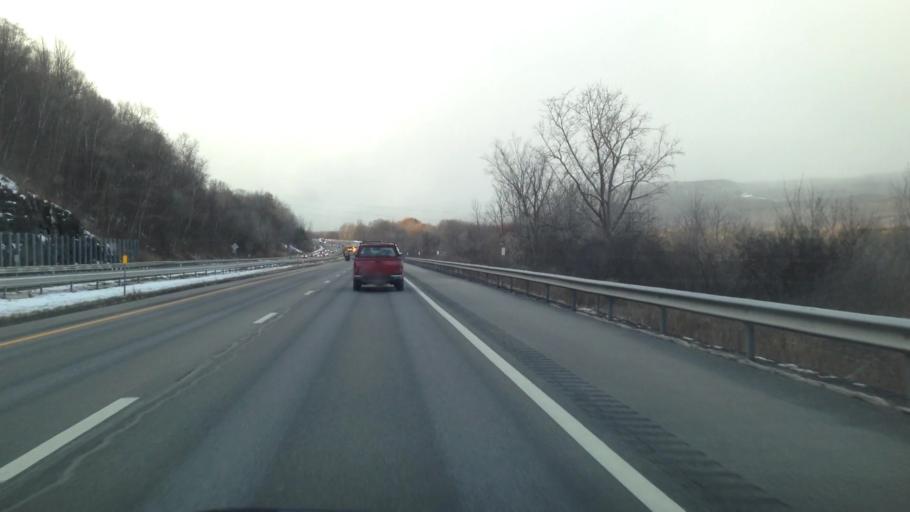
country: US
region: New York
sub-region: Schenectady County
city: Scotia
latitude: 42.8642
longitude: -74.0401
